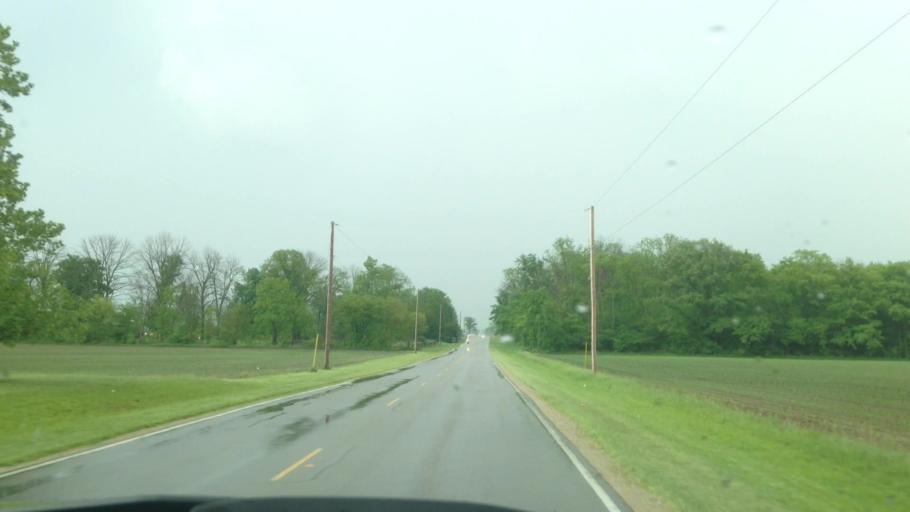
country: US
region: Ohio
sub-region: Darke County
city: Greenville
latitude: 40.1505
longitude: -84.6586
